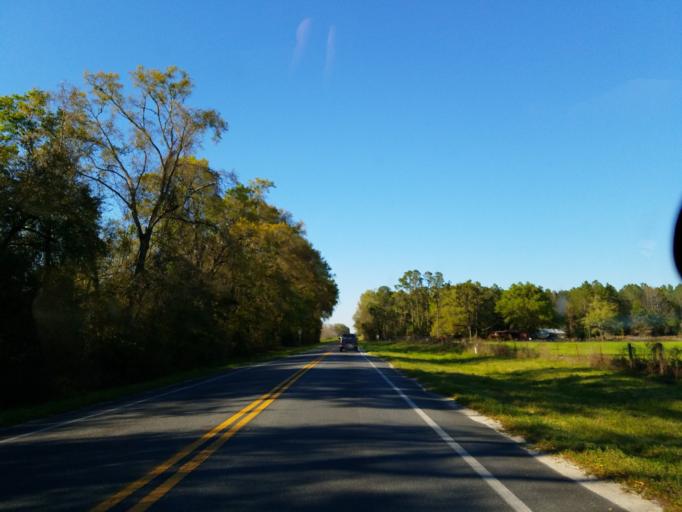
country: US
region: Florida
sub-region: Suwannee County
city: Wellborn
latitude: 29.9543
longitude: -82.8605
